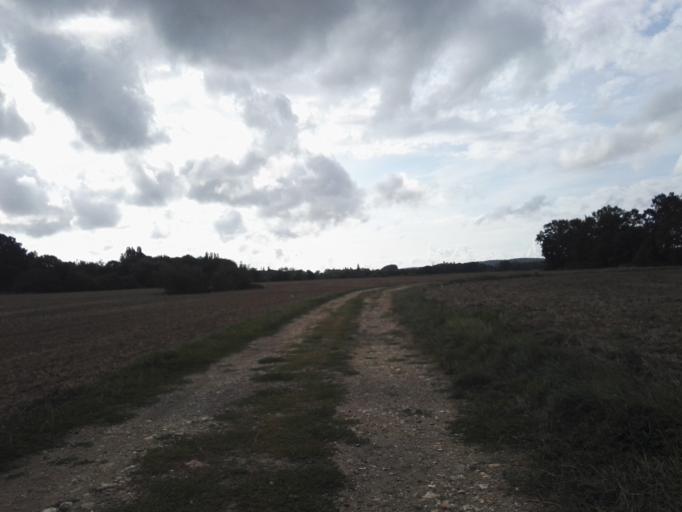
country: FR
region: Haute-Normandie
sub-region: Departement de l'Eure
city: Houlbec-Cocherel
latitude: 49.0640
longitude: 1.3082
